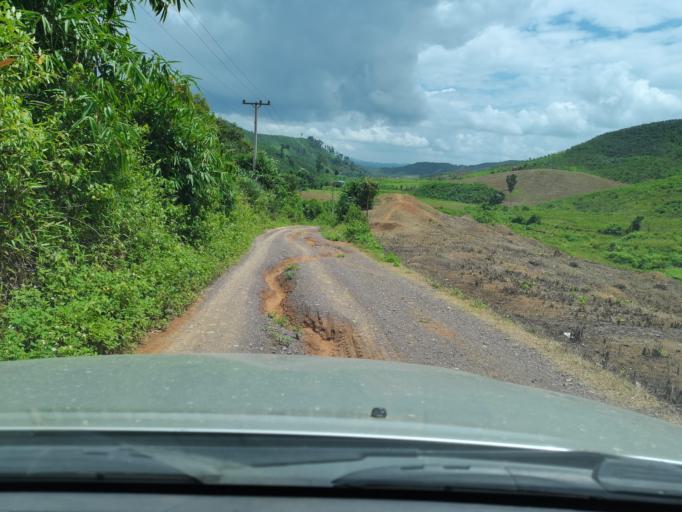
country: LA
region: Loungnamtha
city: Muang Long
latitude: 20.7274
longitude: 101.0141
